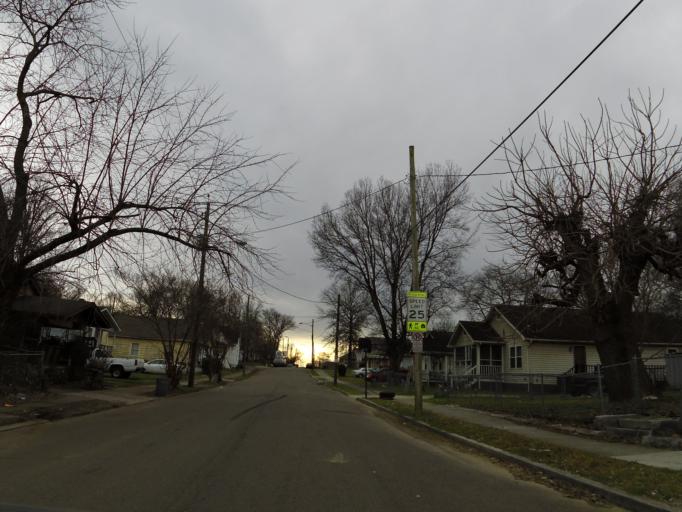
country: US
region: Tennessee
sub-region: Knox County
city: Knoxville
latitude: 35.9703
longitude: -83.9341
